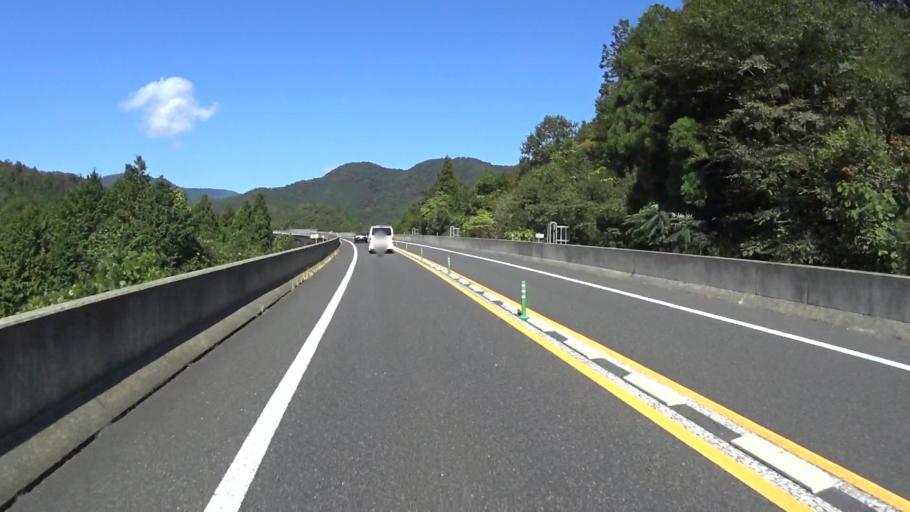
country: JP
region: Kyoto
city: Miyazu
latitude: 35.4462
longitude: 135.1853
